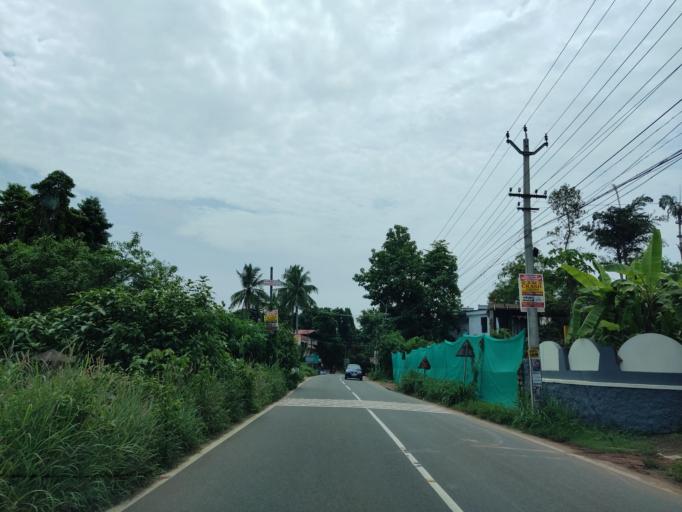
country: IN
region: Kerala
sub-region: Alappuzha
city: Chengannur
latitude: 9.3004
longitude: 76.6275
